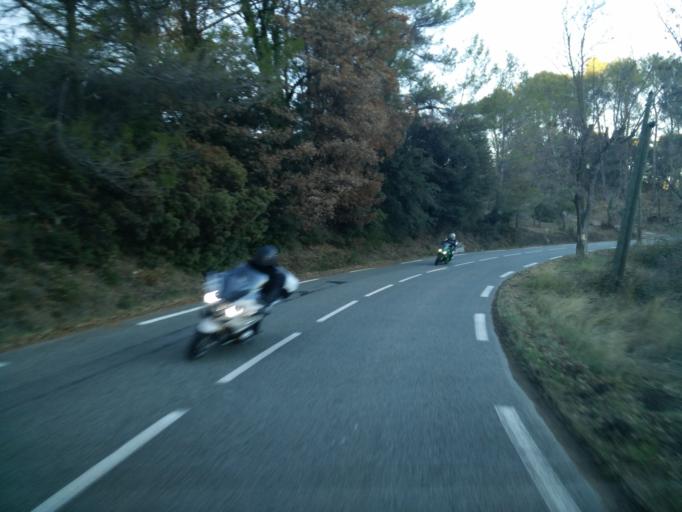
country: FR
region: Provence-Alpes-Cote d'Azur
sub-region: Departement du Var
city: Figanieres
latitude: 43.5406
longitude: 6.5194
